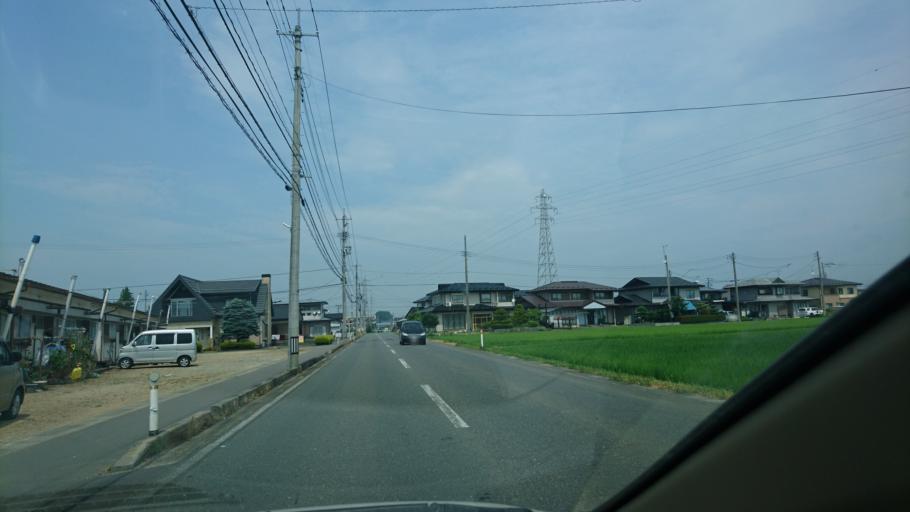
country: JP
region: Iwate
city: Kitakami
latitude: 39.2721
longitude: 141.0933
